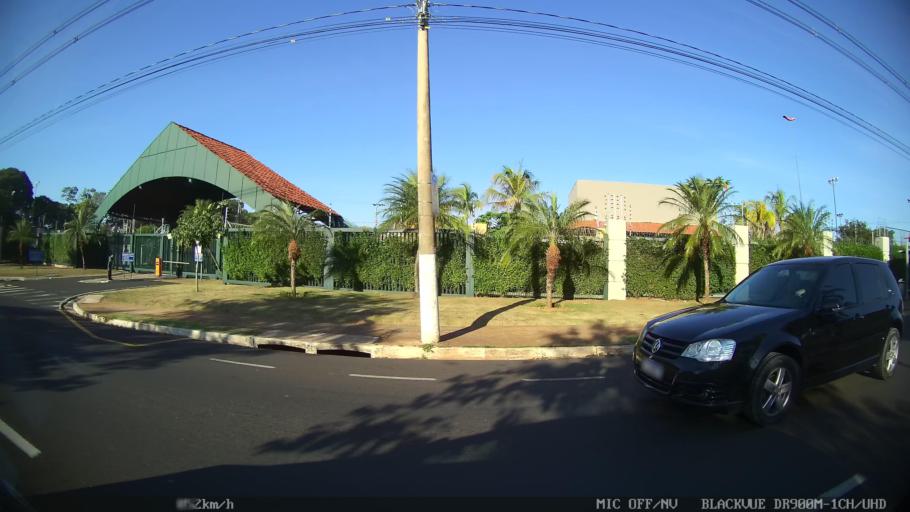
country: BR
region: Sao Paulo
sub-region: Sao Jose Do Rio Preto
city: Sao Jose do Rio Preto
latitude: -20.8495
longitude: -49.4124
